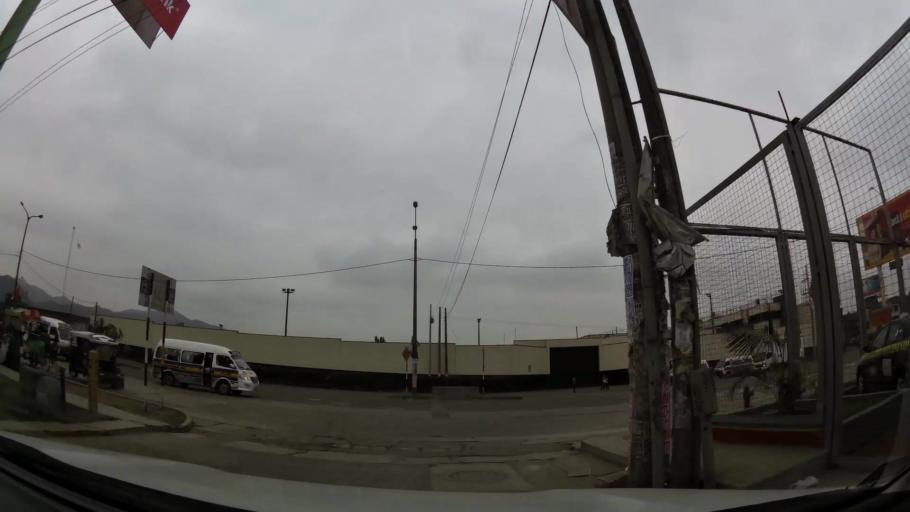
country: PE
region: Lima
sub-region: Lima
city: Vitarte
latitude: -12.0483
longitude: -76.9500
